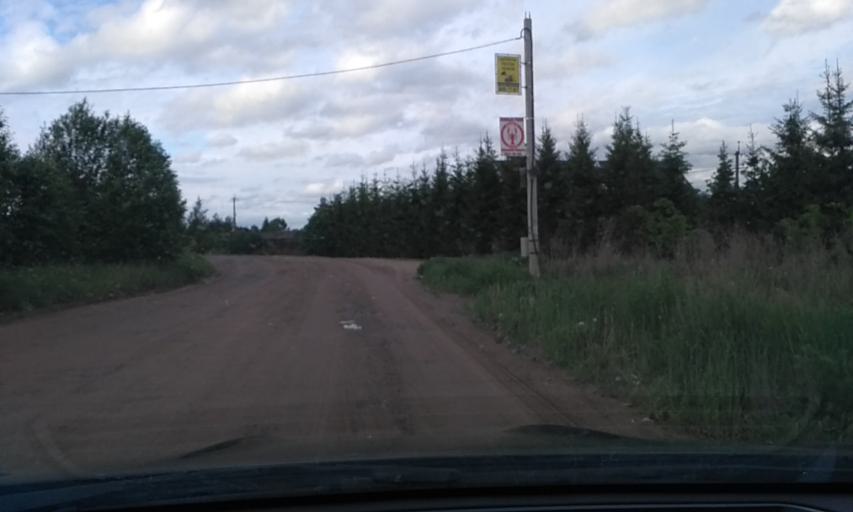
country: RU
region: Leningrad
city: Otradnoye
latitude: 59.7884
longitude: 30.7896
